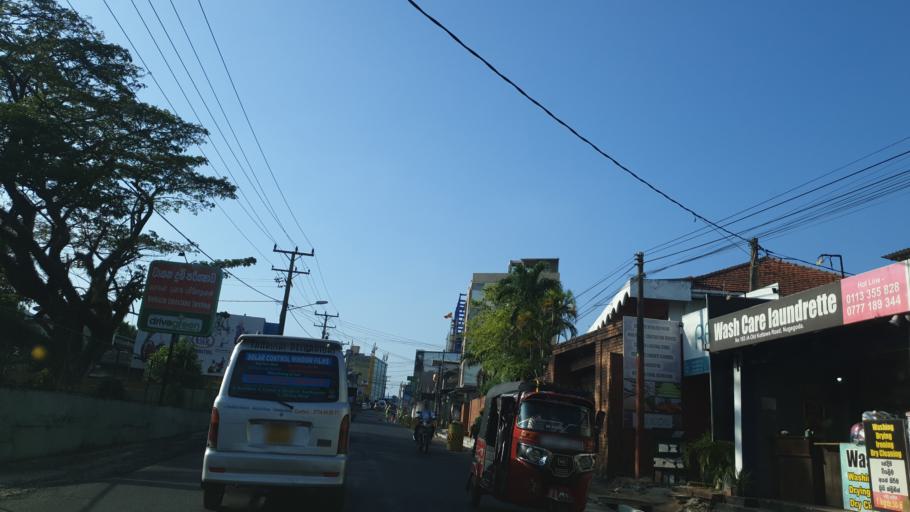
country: LK
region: Western
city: Sri Jayewardenepura Kotte
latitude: 6.8708
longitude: 79.9066
